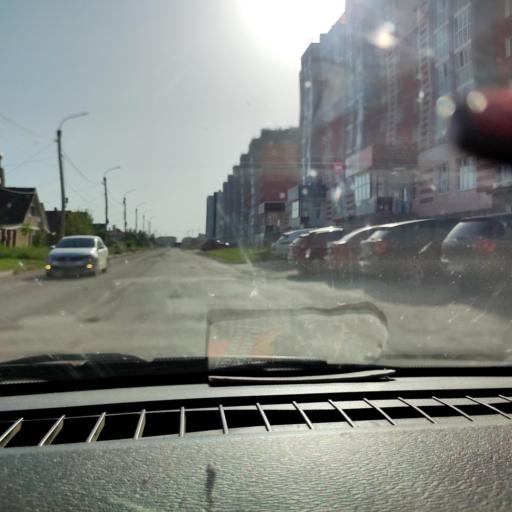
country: RU
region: Bashkortostan
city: Sterlitamak
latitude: 53.6373
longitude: 55.8981
